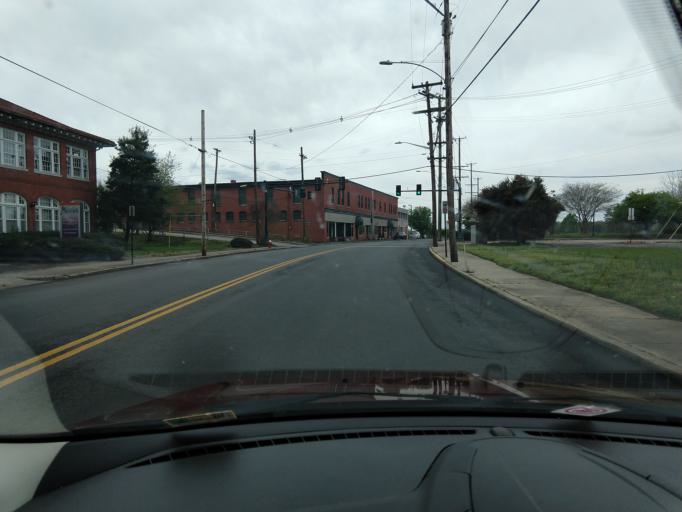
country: US
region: Virginia
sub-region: City of Danville
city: Danville
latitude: 36.5695
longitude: -79.4240
